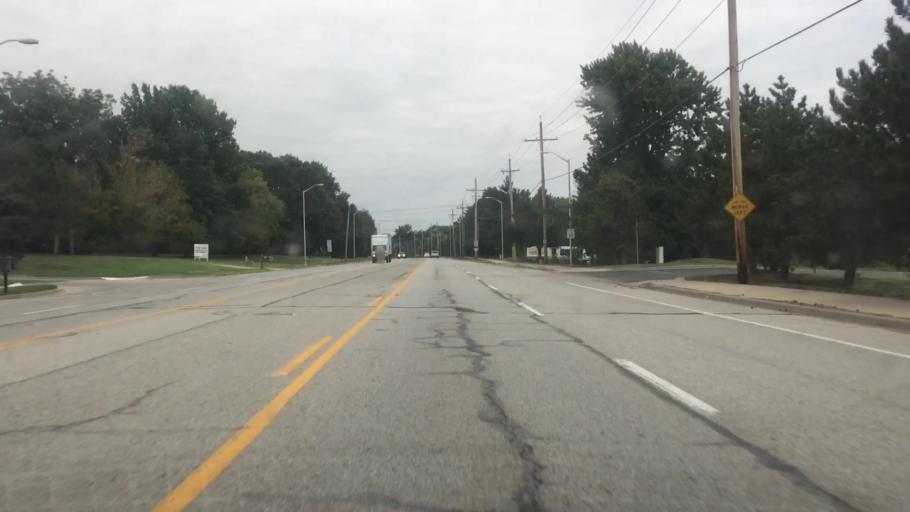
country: US
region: Kansas
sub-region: Johnson County
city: Lenexa
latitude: 38.9988
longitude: -94.7746
